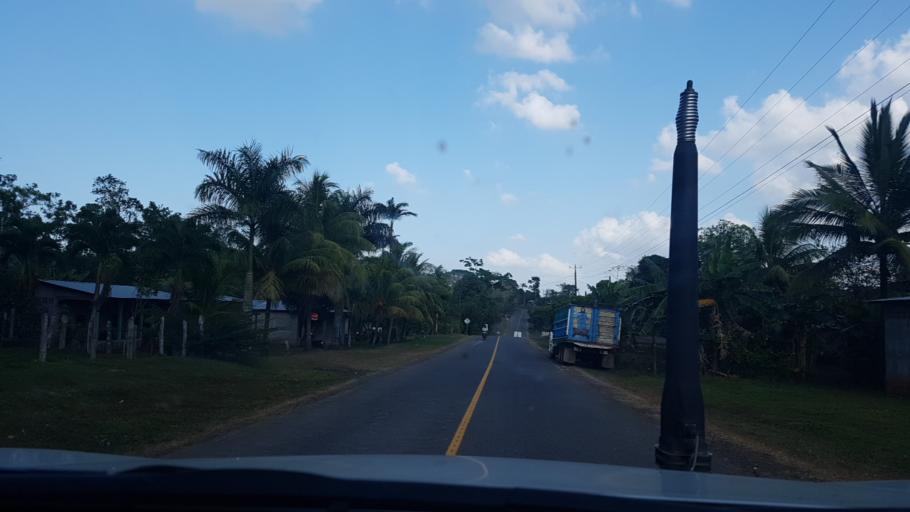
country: NI
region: Atlantico Sur
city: Nueva Guinea
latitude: 11.6935
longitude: -84.4030
